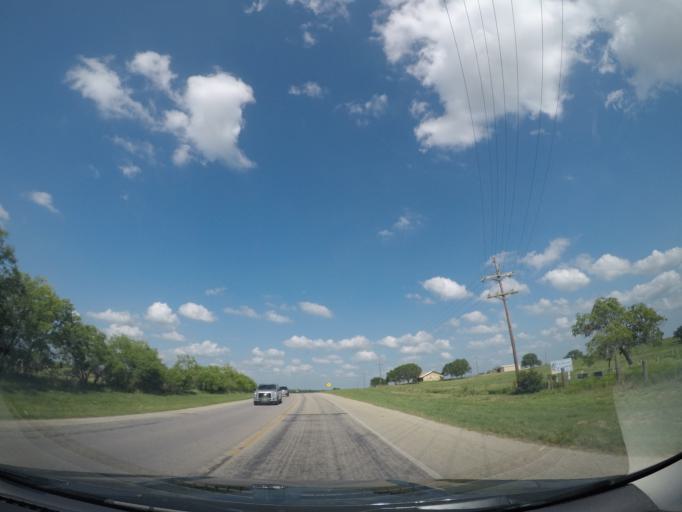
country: US
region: Texas
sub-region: Gonzales County
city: Gonzales
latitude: 29.4954
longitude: -97.5376
